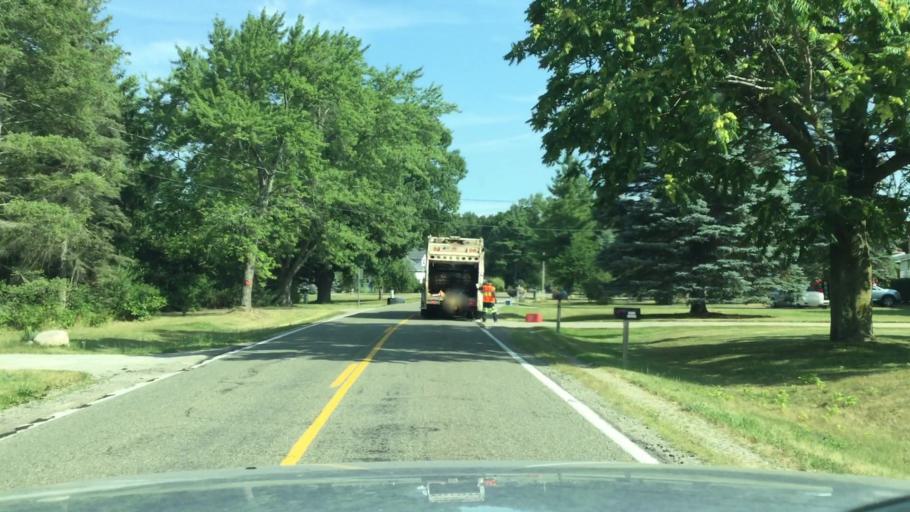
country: US
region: Michigan
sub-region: Genesee County
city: Montrose
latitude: 43.1314
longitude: -83.8591
